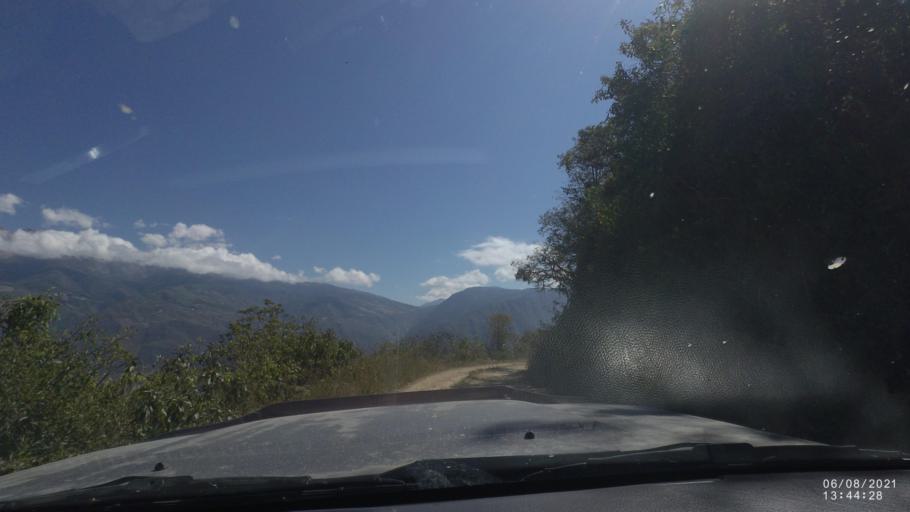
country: BO
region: La Paz
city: Quime
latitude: -16.6752
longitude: -66.7325
